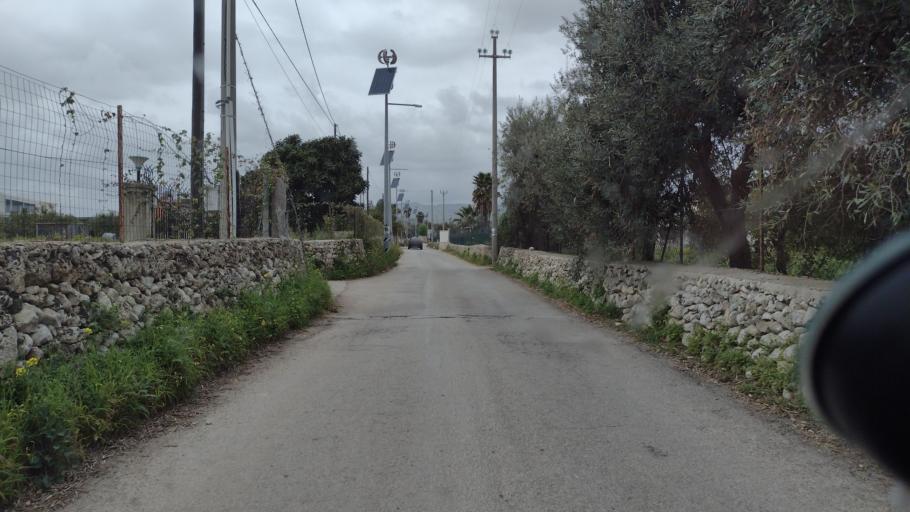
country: IT
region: Sicily
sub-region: Provincia di Siracusa
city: Avola
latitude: 36.8920
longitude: 15.1173
